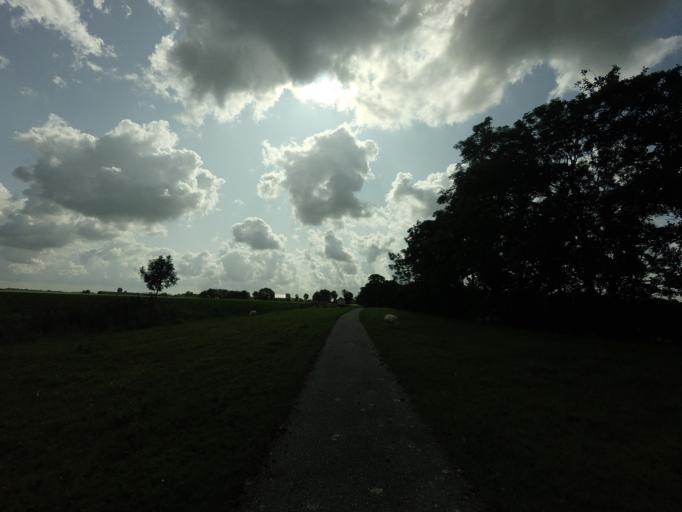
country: NL
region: Friesland
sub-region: Gemeente Het Bildt
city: Minnertsga
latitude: 53.2601
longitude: 5.5953
